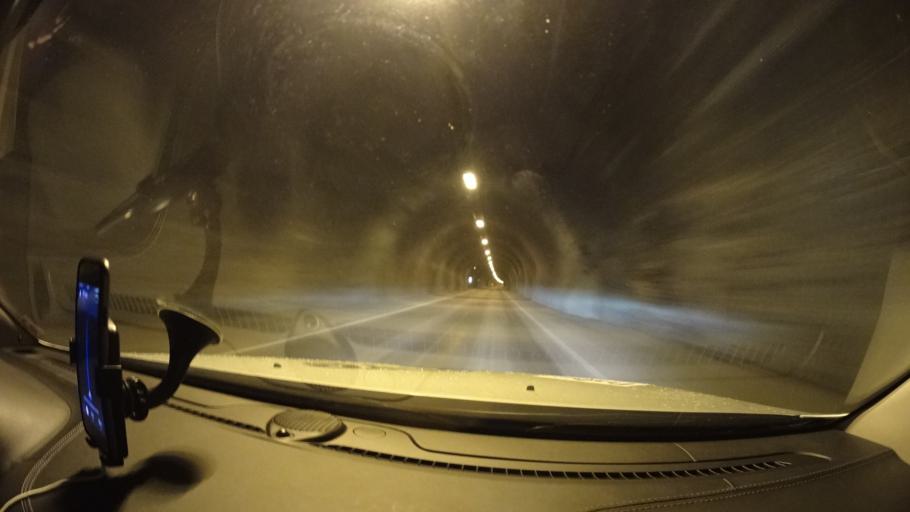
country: NO
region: Finnmark Fylke
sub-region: Nordkapp
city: Honningsvag
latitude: 70.9930
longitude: 25.9275
